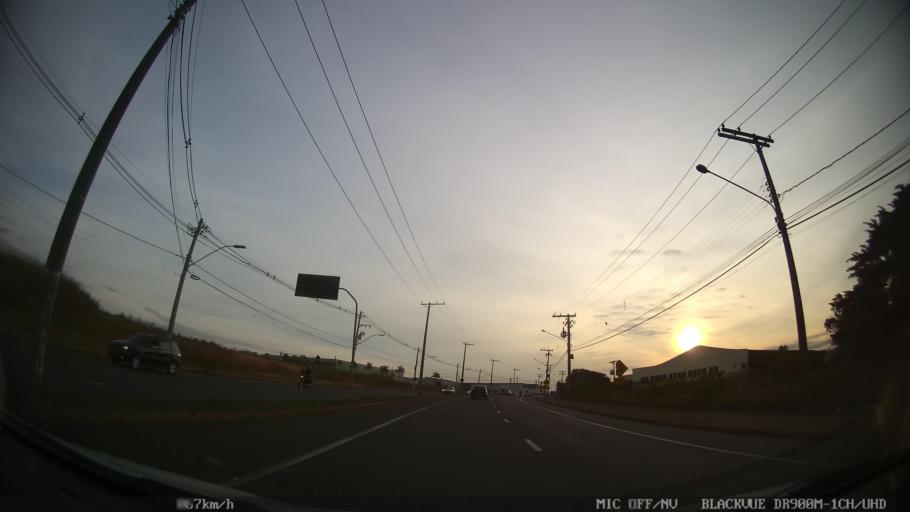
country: BR
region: Sao Paulo
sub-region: Limeira
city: Limeira
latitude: -22.5889
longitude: -47.3861
